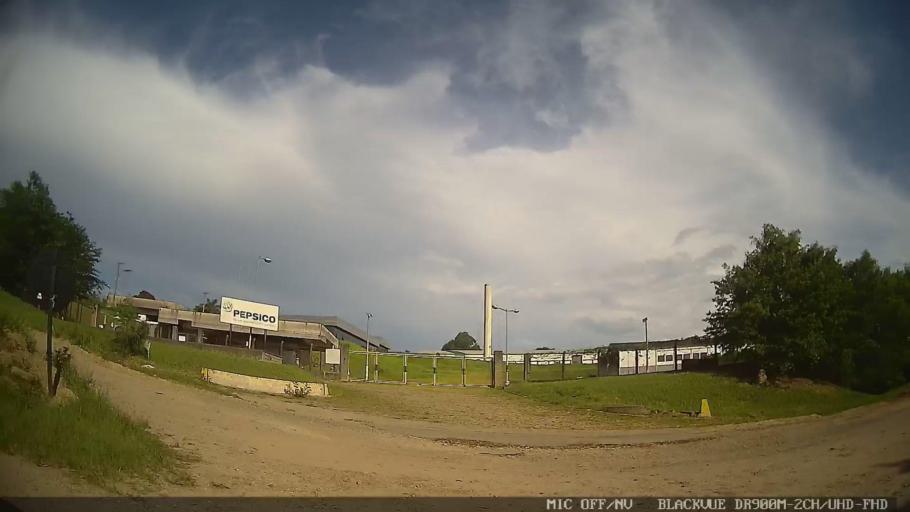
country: BR
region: Sao Paulo
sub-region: Tiete
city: Tiete
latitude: -23.0996
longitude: -47.6908
